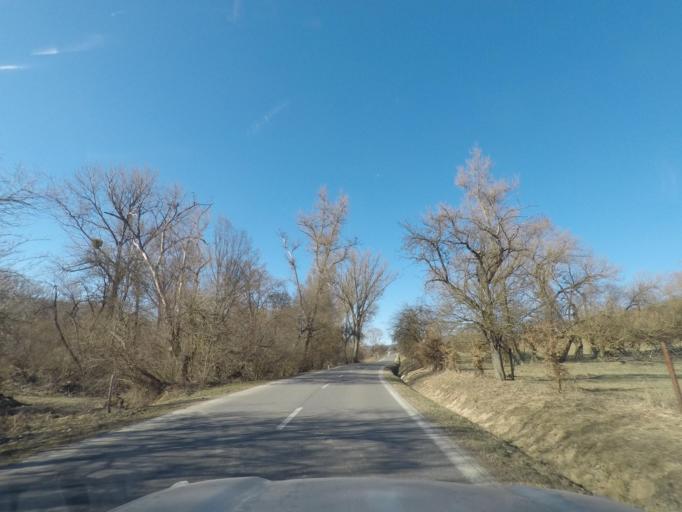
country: SK
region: Presovsky
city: Snina
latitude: 49.0547
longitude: 22.1721
